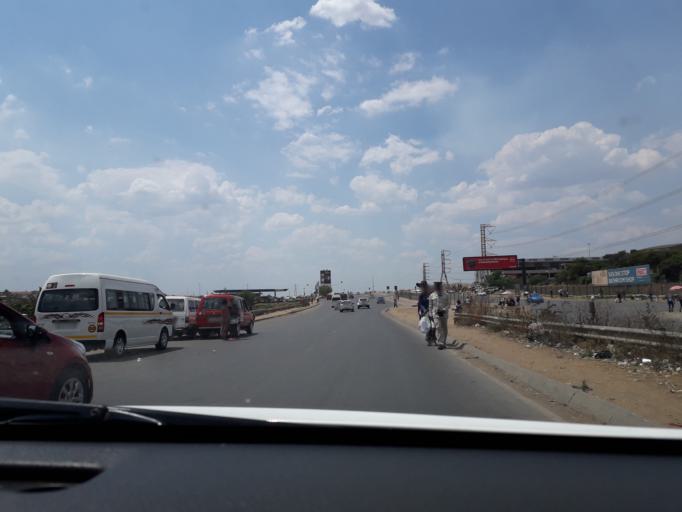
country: ZA
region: Gauteng
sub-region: Ekurhuleni Metropolitan Municipality
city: Tembisa
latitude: -26.0368
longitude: 28.1907
